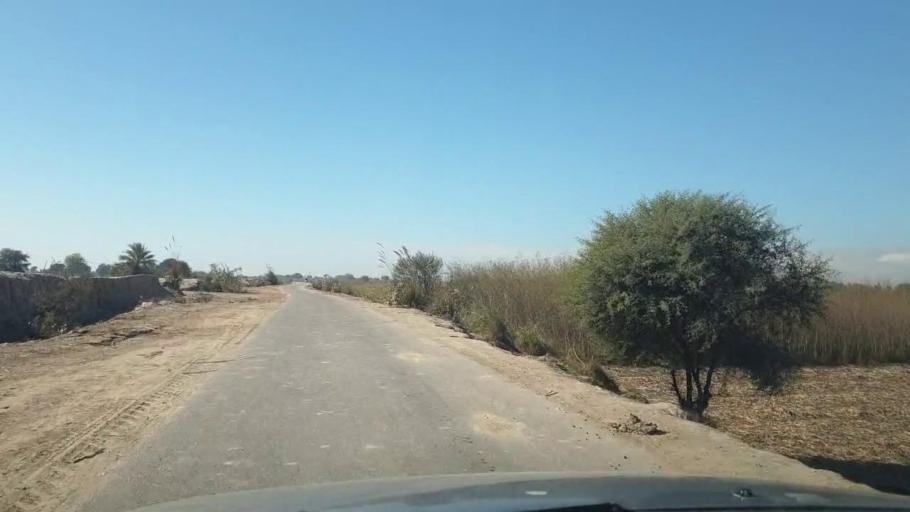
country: PK
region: Sindh
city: Ghotki
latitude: 28.0271
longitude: 69.2739
